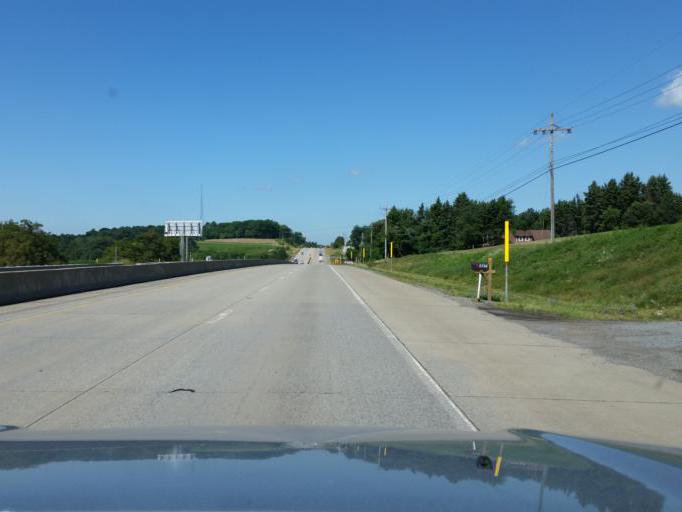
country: US
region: Pennsylvania
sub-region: Cambria County
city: Vinco
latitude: 40.4420
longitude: -78.9500
